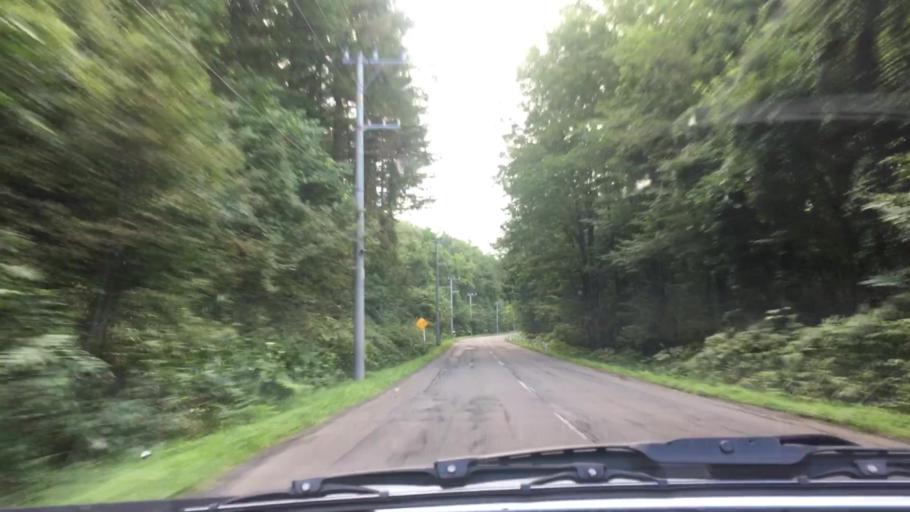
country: JP
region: Hokkaido
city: Otofuke
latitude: 43.1444
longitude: 142.8777
